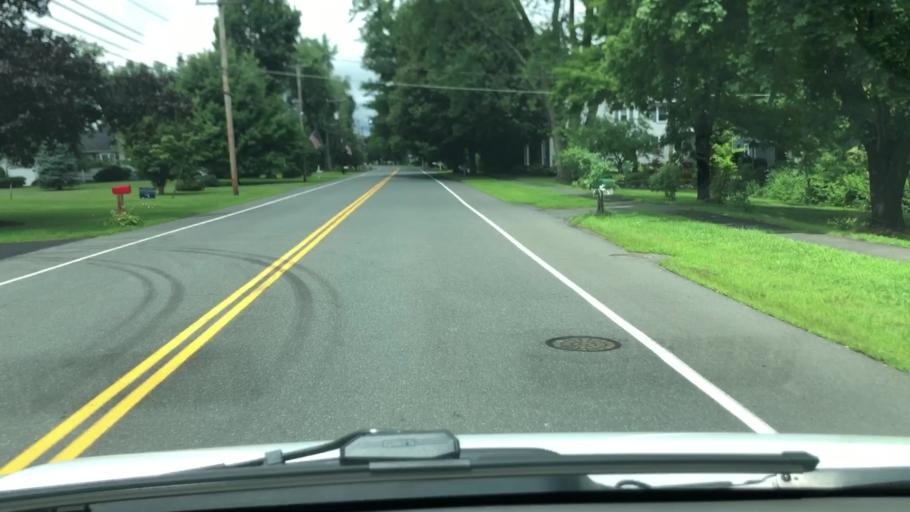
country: US
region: Massachusetts
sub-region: Franklin County
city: South Deerfield
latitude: 42.4901
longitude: -72.6057
